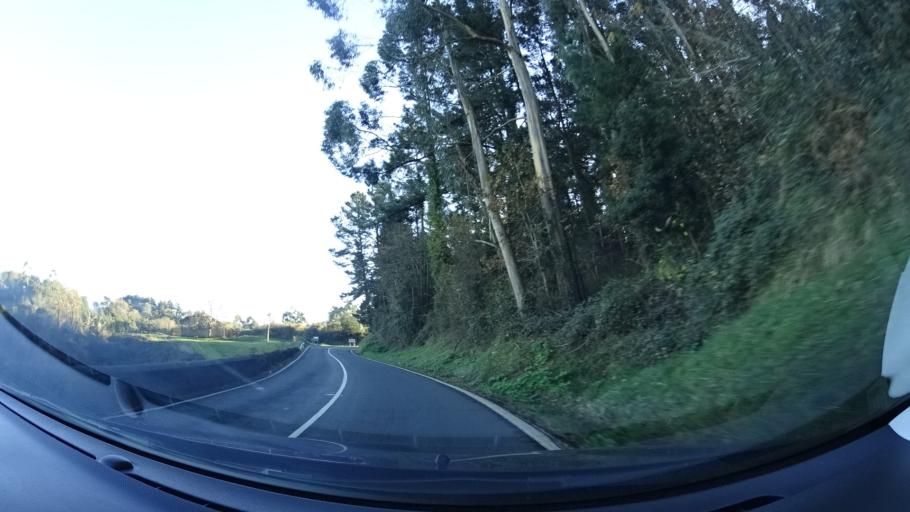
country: ES
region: Basque Country
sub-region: Bizkaia
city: Lekeitio
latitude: 43.3587
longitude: -2.5237
